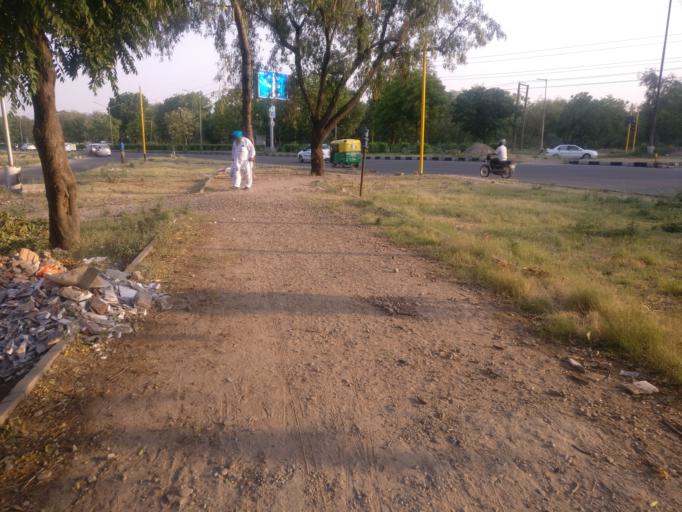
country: IN
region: Punjab
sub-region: Ajitgarh
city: Mohali
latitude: 30.7310
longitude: 76.7316
